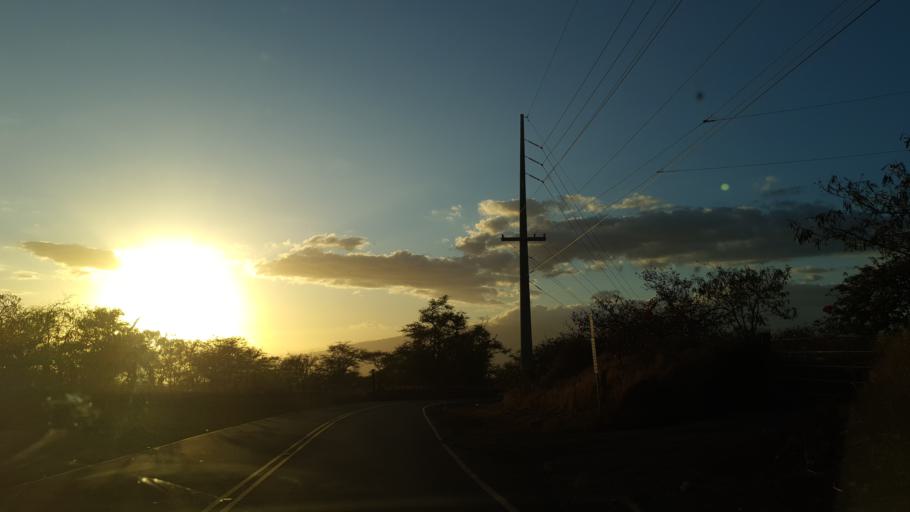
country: US
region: Hawaii
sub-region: Maui County
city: Pukalani
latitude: 20.7945
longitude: -156.3655
